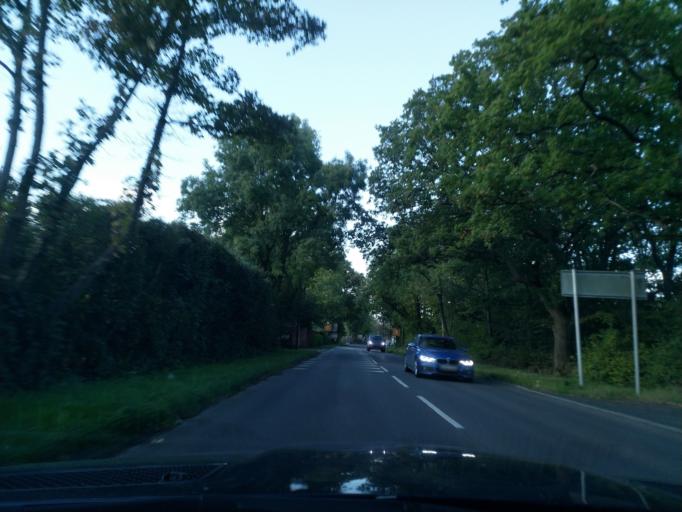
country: GB
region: England
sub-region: Solihull
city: Cheswick Green
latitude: 52.3476
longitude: -1.7768
